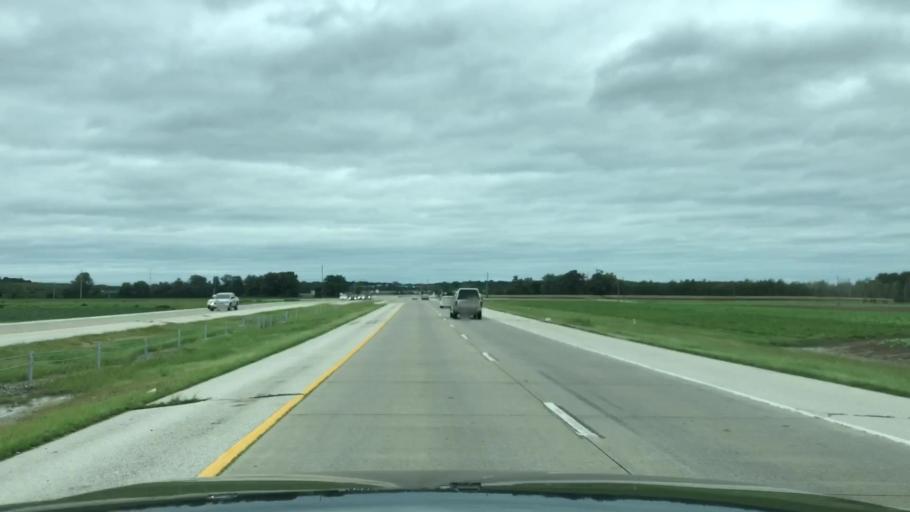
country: US
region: Missouri
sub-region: Saint Charles County
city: Saint Charles
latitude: 38.7199
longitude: -90.4984
